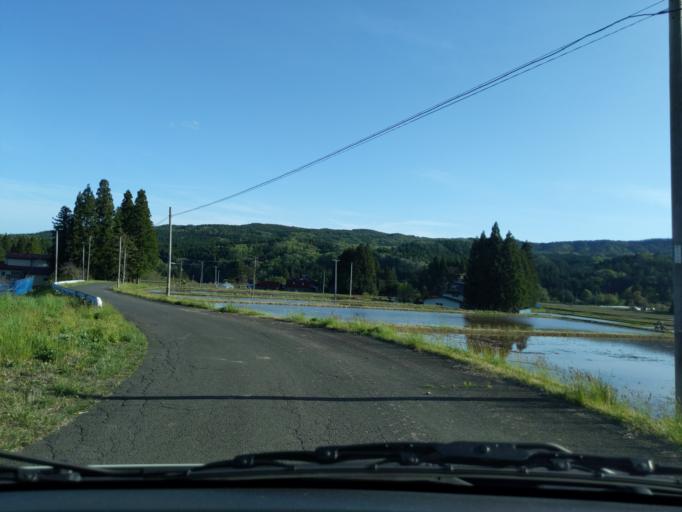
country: JP
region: Iwate
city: Ichinoseki
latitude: 38.8791
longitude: 140.8920
